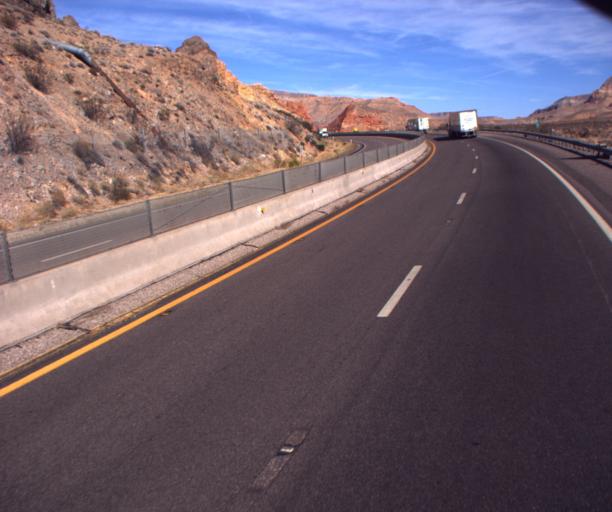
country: US
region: Arizona
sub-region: Mohave County
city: Beaver Dam
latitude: 36.9414
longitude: -113.8160
